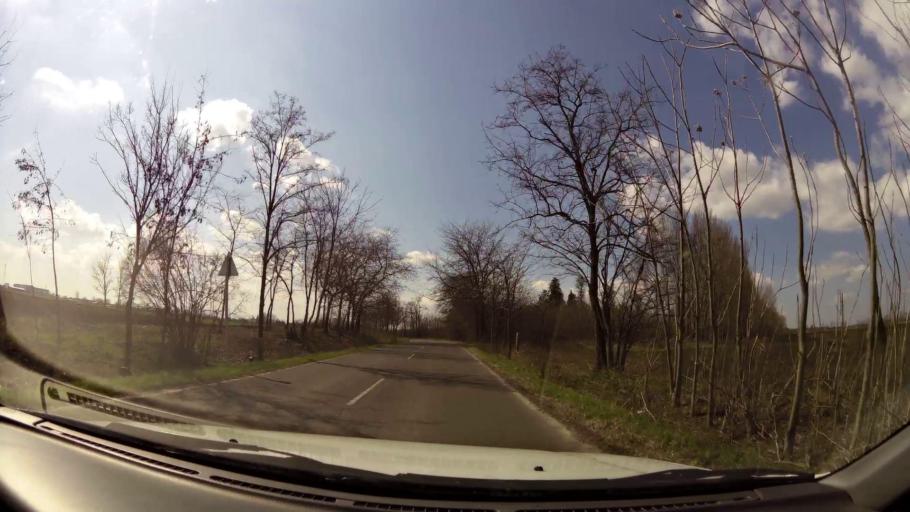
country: HU
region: Pest
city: Tapioszele
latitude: 47.3350
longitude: 19.8956
